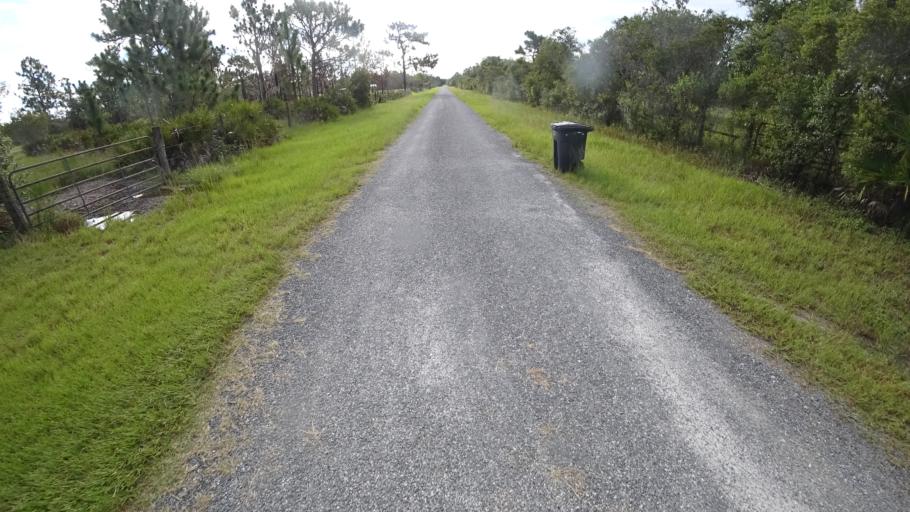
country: US
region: Florida
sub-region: Sarasota County
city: Fruitville
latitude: 27.4088
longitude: -82.2854
